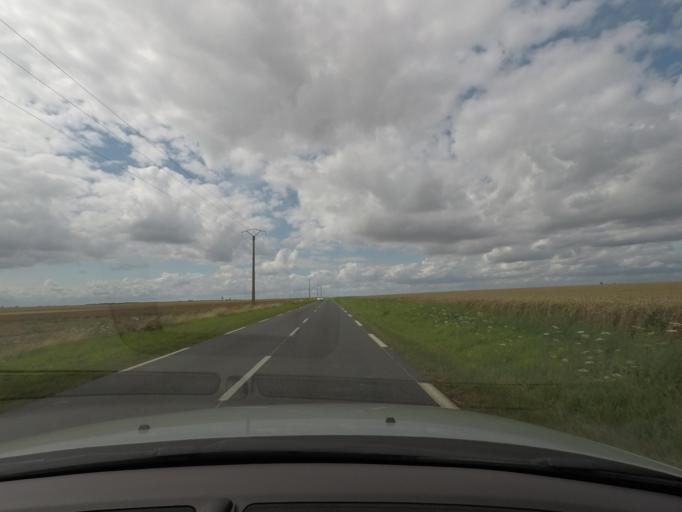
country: FR
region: Haute-Normandie
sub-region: Departement de l'Eure
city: Les Andelys
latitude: 49.2192
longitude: 1.4505
